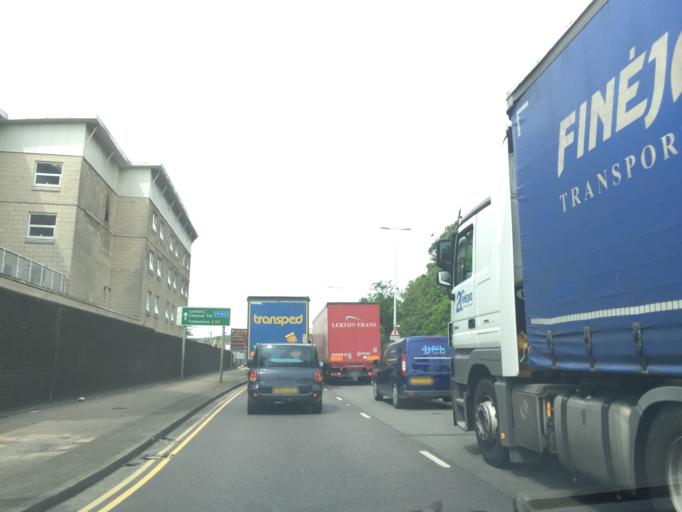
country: GB
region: England
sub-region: Kent
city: Dover
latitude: 51.1253
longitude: 1.3218
